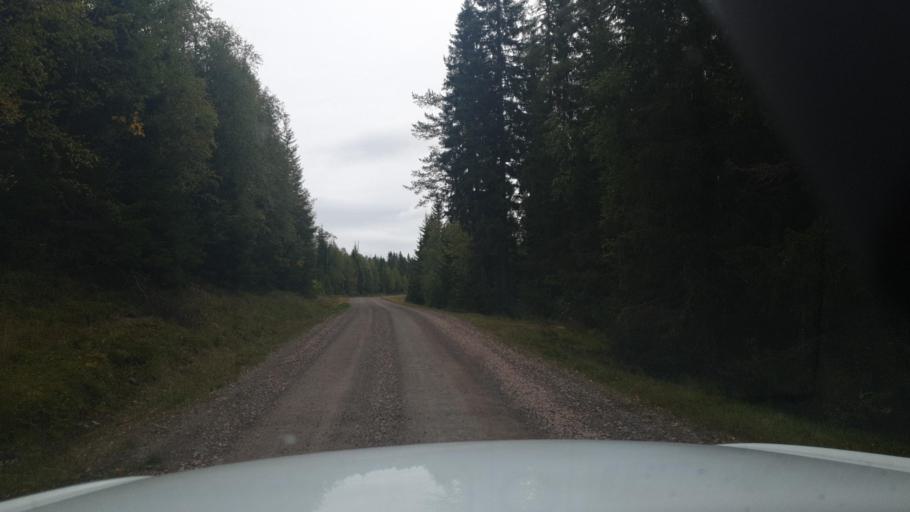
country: SE
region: Vaermland
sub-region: Eda Kommun
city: Charlottenberg
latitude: 60.1271
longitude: 12.5951
